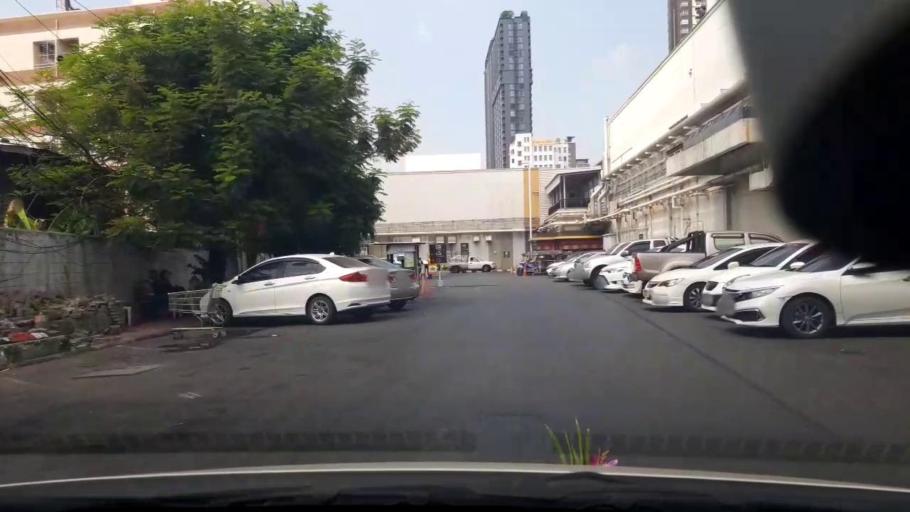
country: TH
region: Bangkok
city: Bang Sue
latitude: 13.8261
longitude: 100.5283
